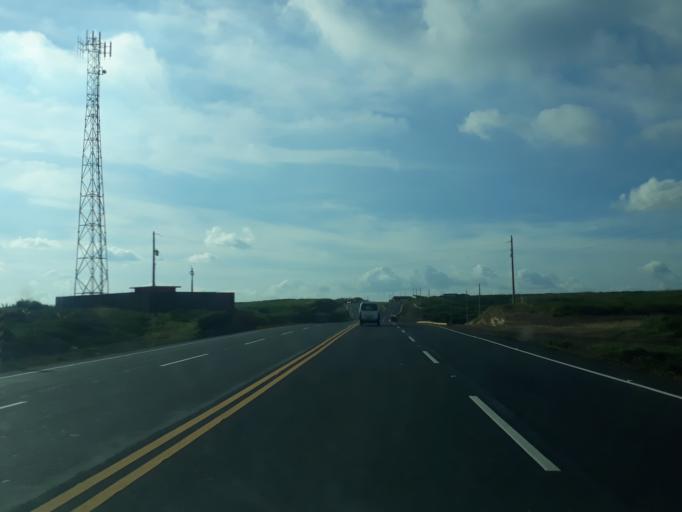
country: NI
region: Managua
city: El Crucero
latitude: 11.9332
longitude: -86.2906
